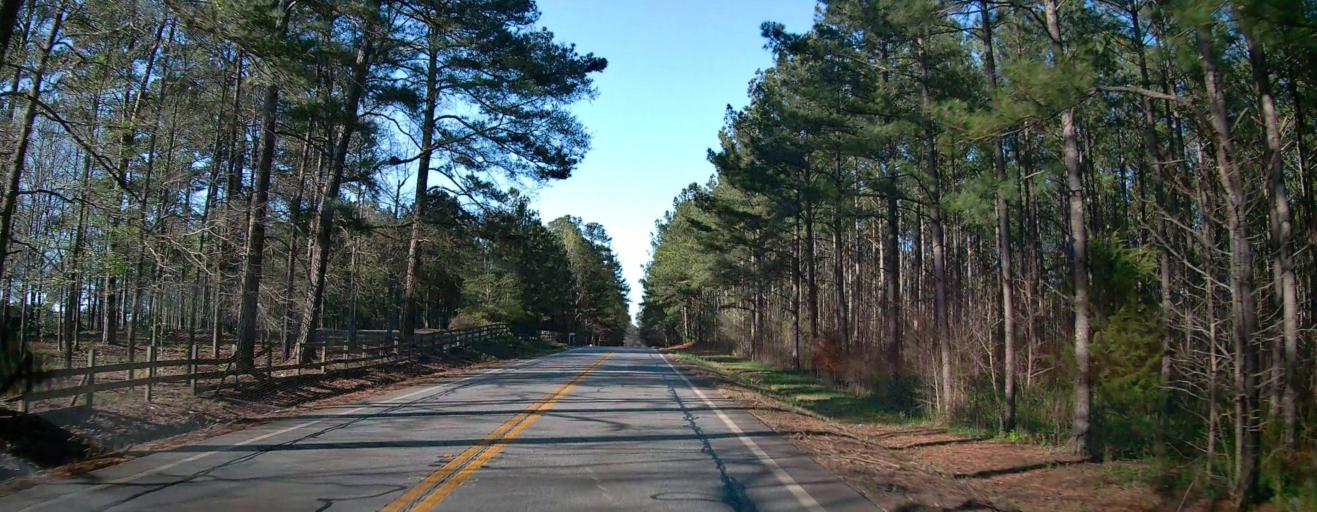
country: US
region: Georgia
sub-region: Butts County
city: Indian Springs
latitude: 33.2165
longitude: -83.9308
